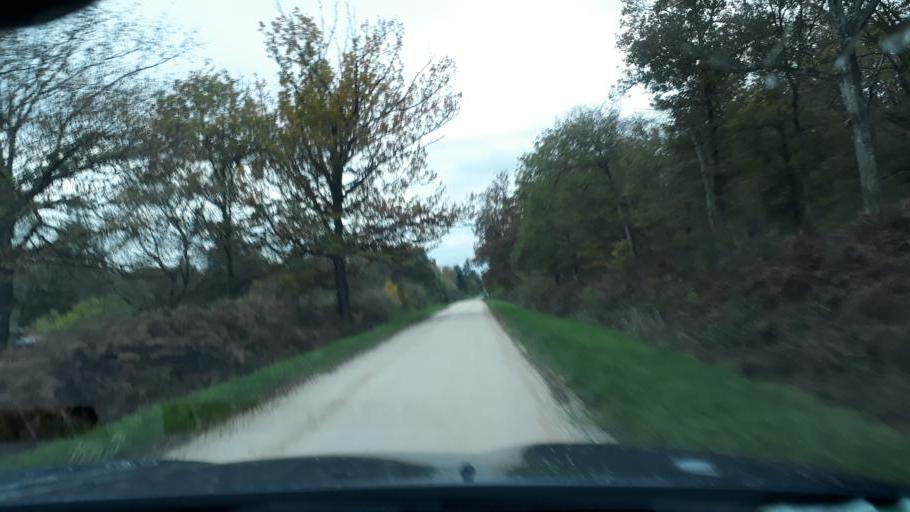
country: FR
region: Centre
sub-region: Departement du Loiret
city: Bouzy-la-Foret
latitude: 47.8194
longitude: 2.4159
